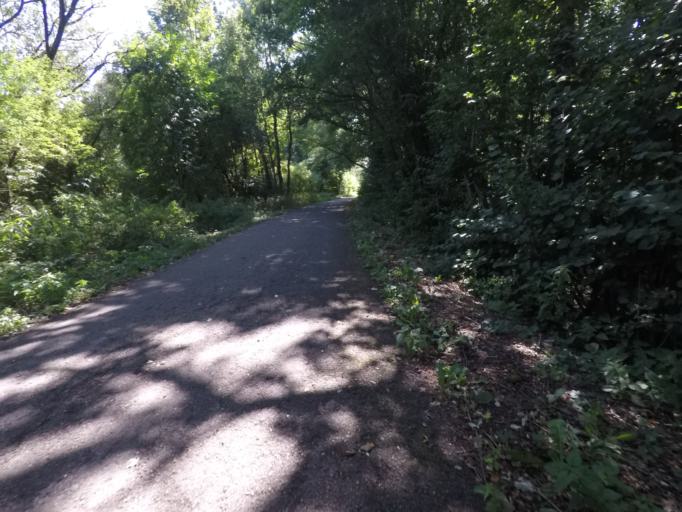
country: LU
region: Luxembourg
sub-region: Canton de Capellen
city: Clemency
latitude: 49.6125
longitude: 5.8774
